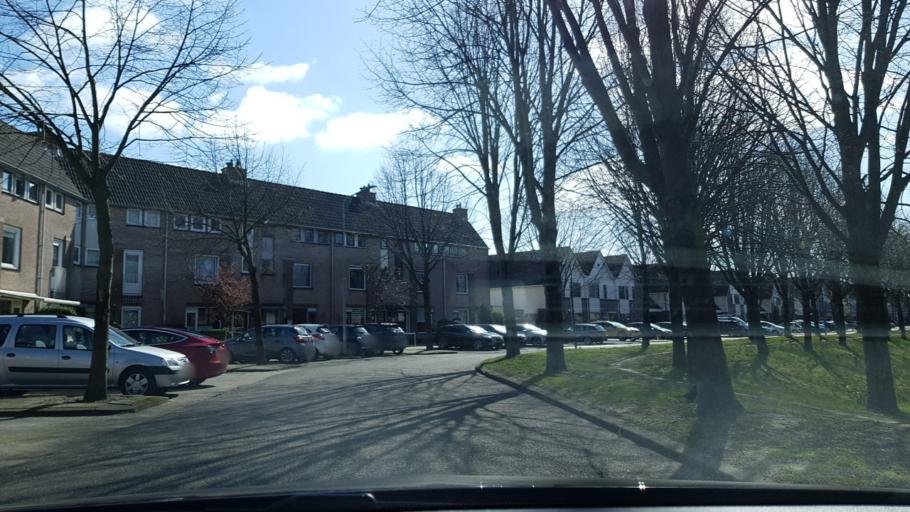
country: NL
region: North Holland
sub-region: Gemeente Haarlemmermeer
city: Hoofddorp
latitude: 52.2963
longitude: 4.6748
